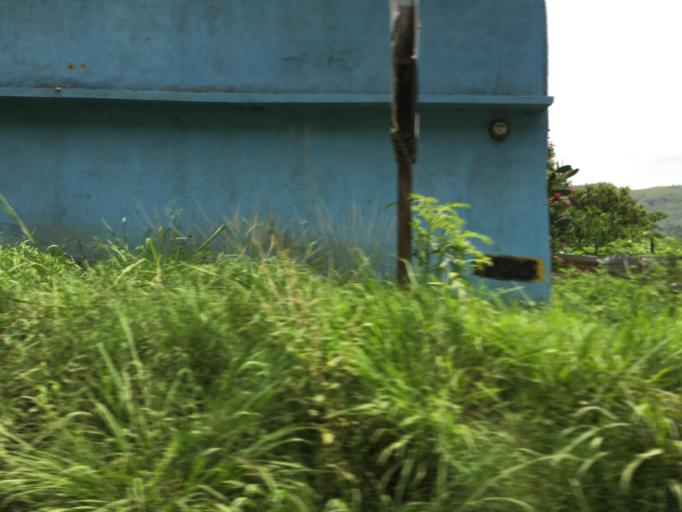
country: GT
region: Guatemala
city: Amatitlan
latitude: 14.4709
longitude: -90.6035
